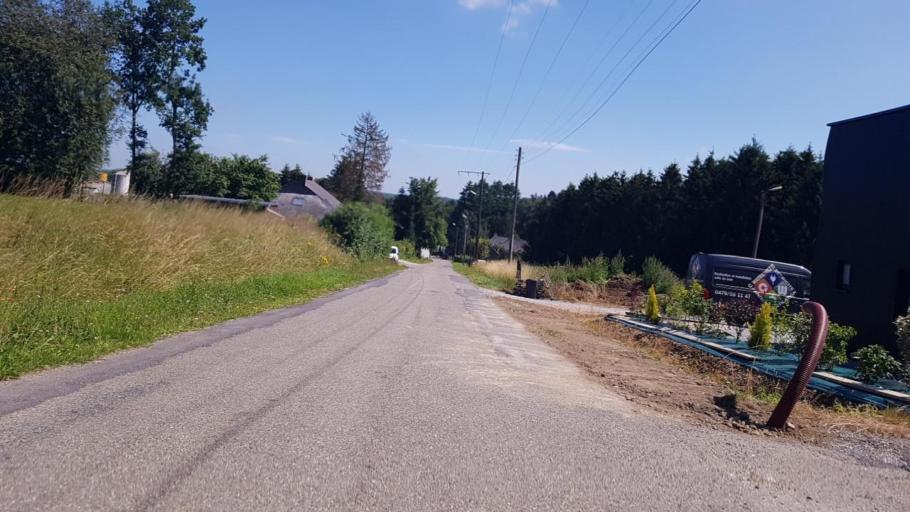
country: BE
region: Wallonia
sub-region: Province du Hainaut
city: Momignies
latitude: 50.0412
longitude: 4.2041
